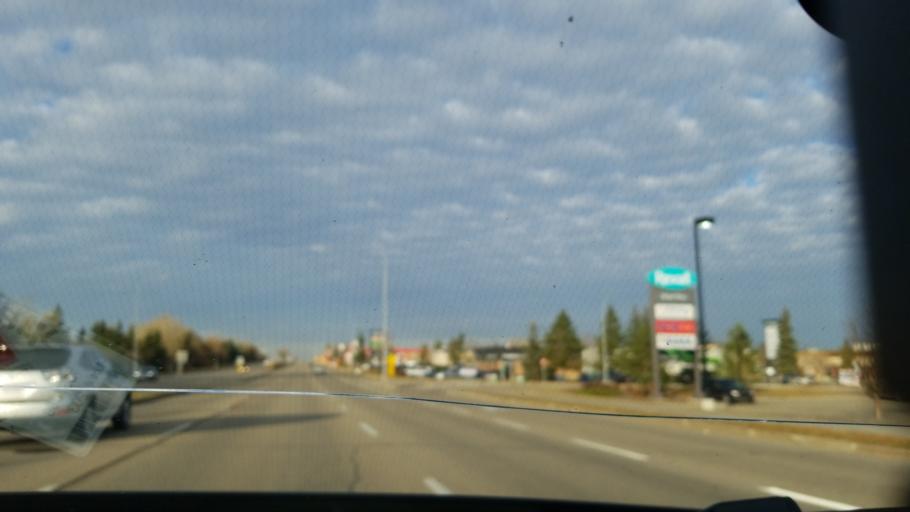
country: CA
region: Alberta
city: Sherwood Park
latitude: 53.5413
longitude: -113.3063
